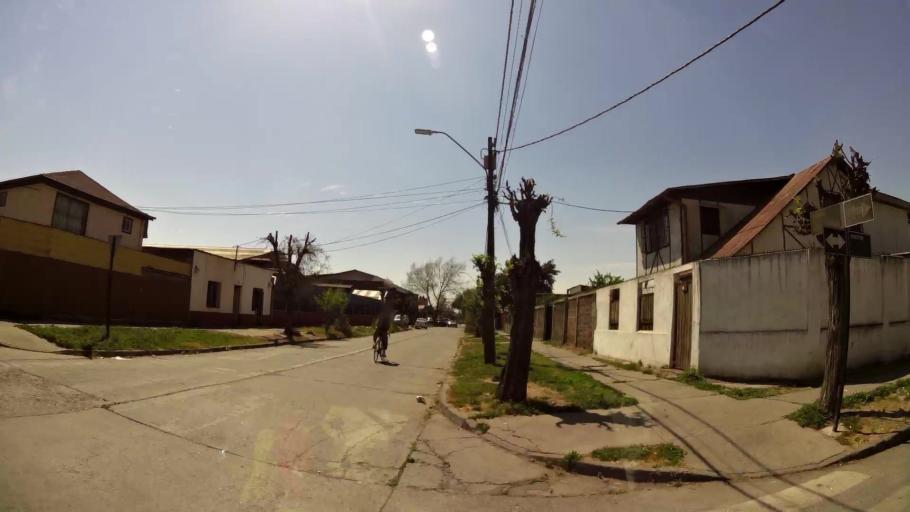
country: CL
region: Santiago Metropolitan
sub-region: Provincia de Santiago
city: La Pintana
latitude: -33.5298
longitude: -70.6510
